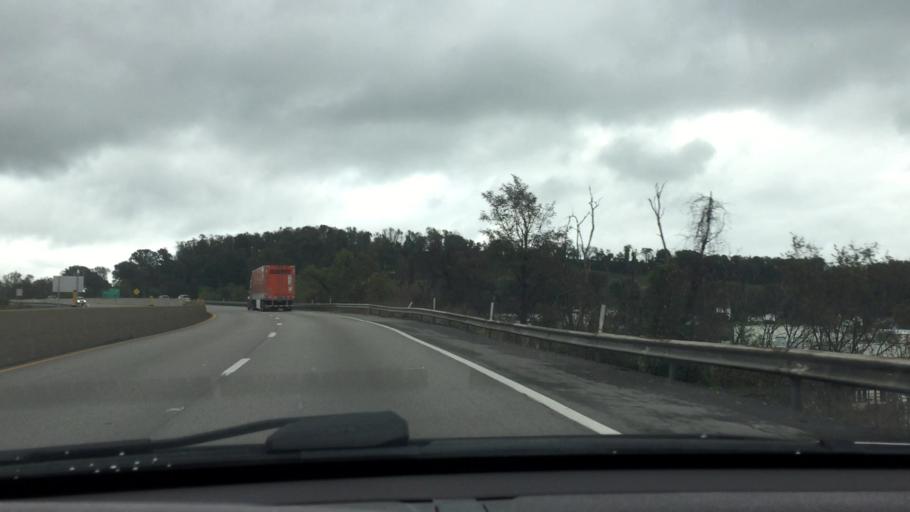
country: US
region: Pennsylvania
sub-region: Westmoreland County
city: Lynnwood-Pricedale
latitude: 40.1399
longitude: -79.8260
